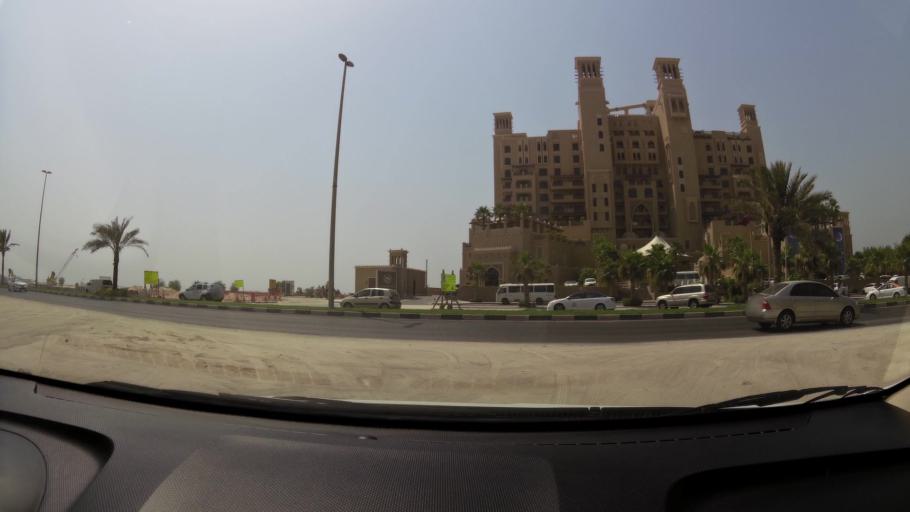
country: AE
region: Ajman
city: Ajman
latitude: 25.3950
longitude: 55.4234
